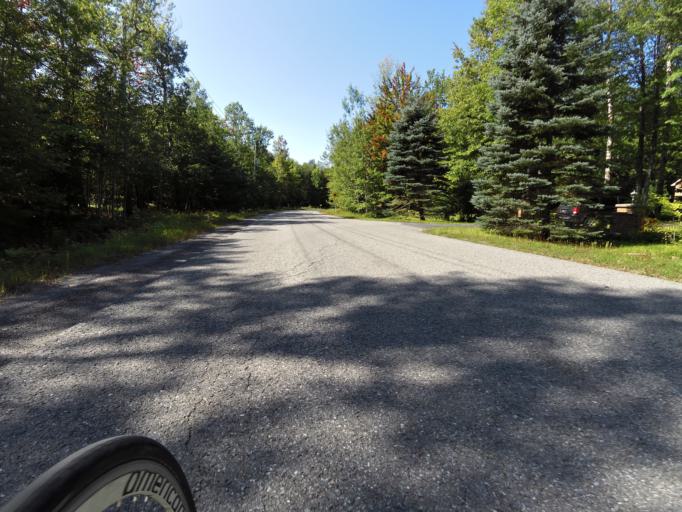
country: CA
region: Ontario
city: Bells Corners
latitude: 45.3777
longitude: -76.0413
